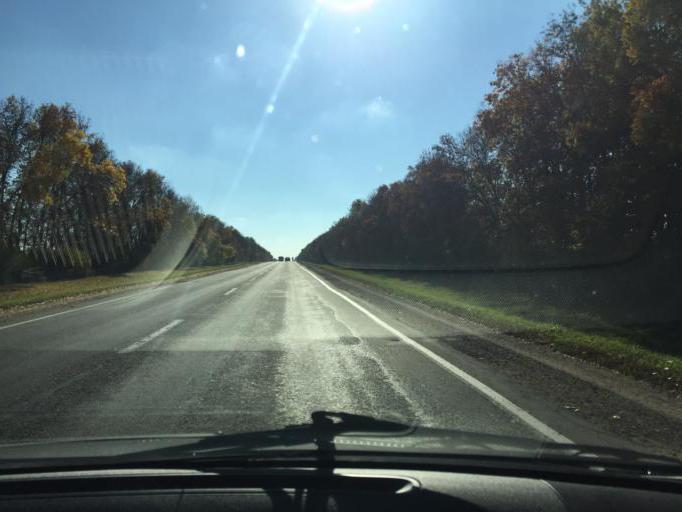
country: BY
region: Minsk
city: Slutsk
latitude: 52.9673
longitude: 27.4997
